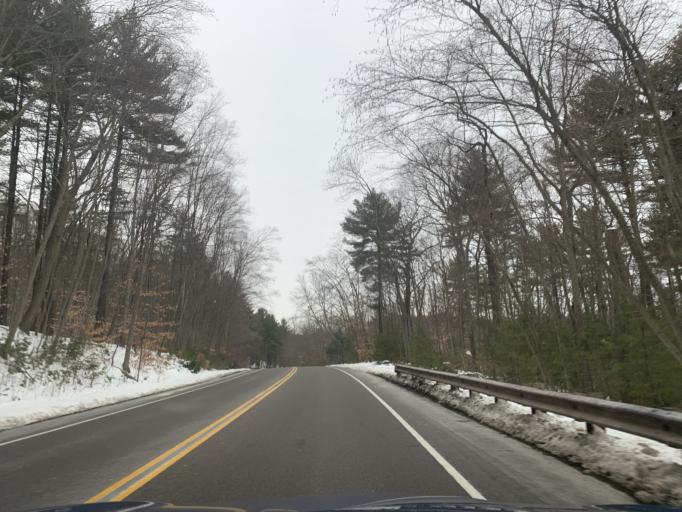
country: US
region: Massachusetts
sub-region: Norfolk County
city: Milton
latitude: 42.2222
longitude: -71.0910
